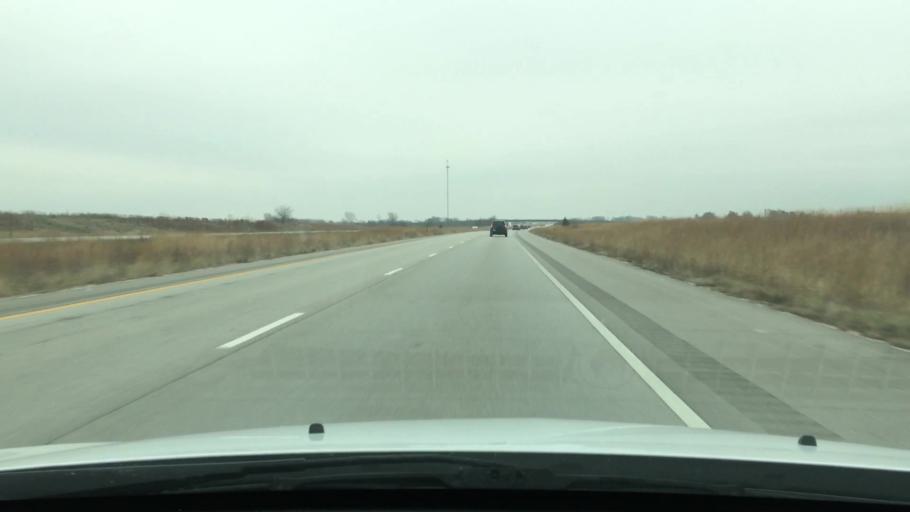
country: US
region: Illinois
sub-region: Morgan County
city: Jacksonville
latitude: 39.7383
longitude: -90.0920
